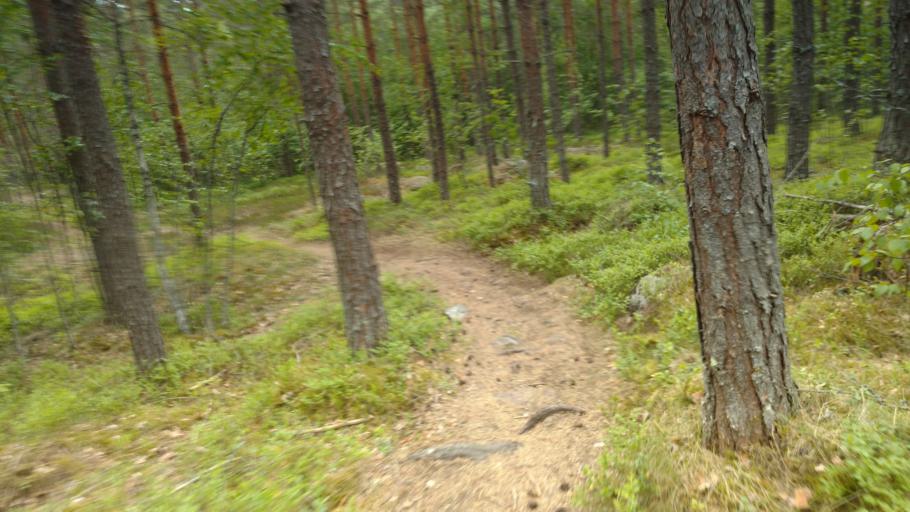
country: FI
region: Uusimaa
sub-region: Raaseporin
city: Pohja
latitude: 60.1110
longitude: 23.5523
